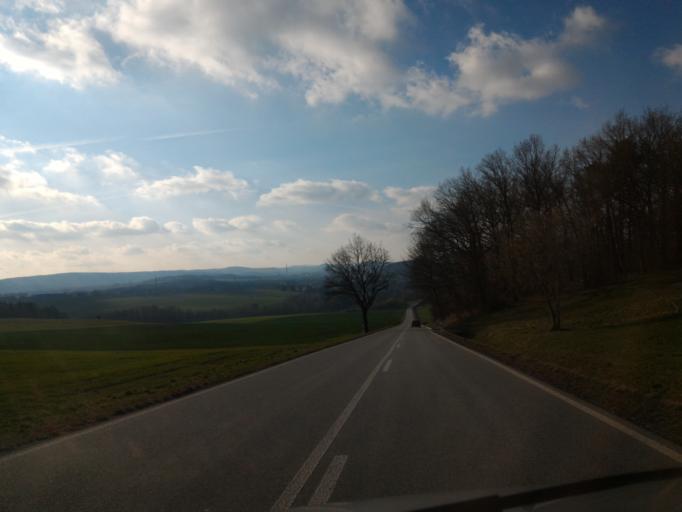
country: DE
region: Saxony
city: Grossschonau
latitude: 50.8855
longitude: 14.6986
